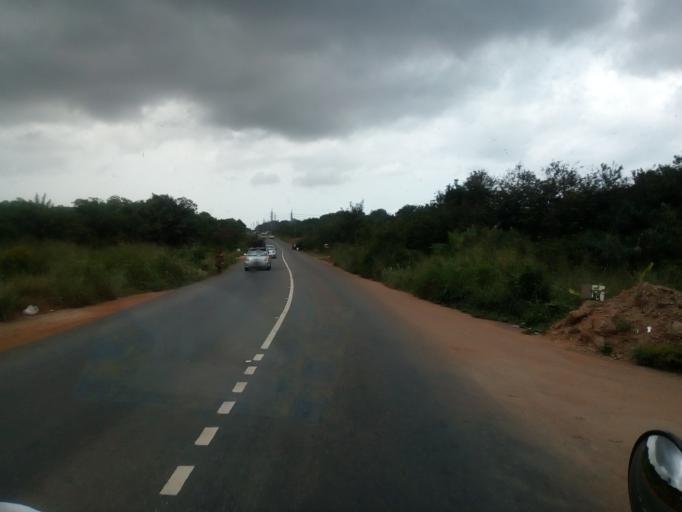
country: GH
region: Greater Accra
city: Dome
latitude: 5.6459
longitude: -0.2049
